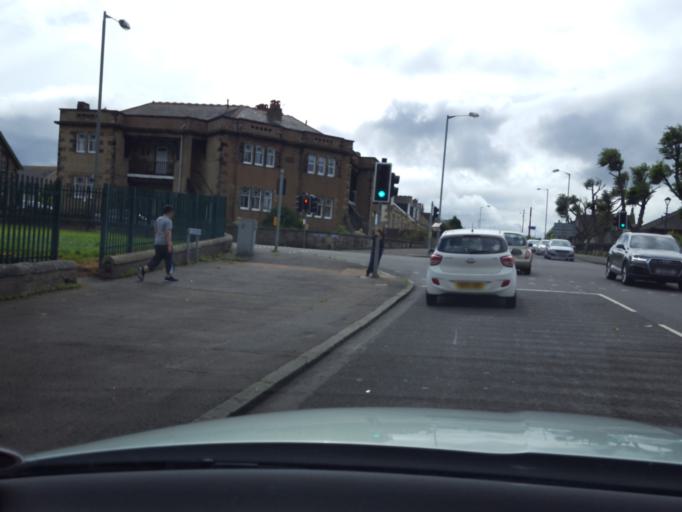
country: GB
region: Scotland
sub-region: Falkirk
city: Bo'ness
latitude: 56.0115
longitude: -3.6112
